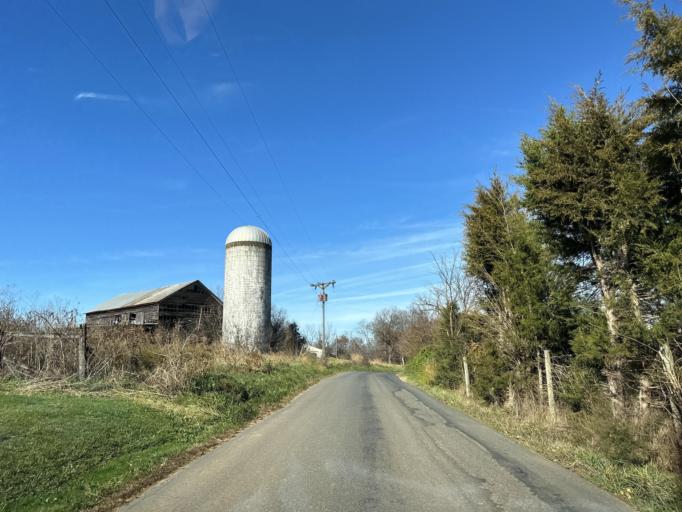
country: US
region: Virginia
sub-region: Augusta County
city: Weyers Cave
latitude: 38.2203
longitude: -78.9218
